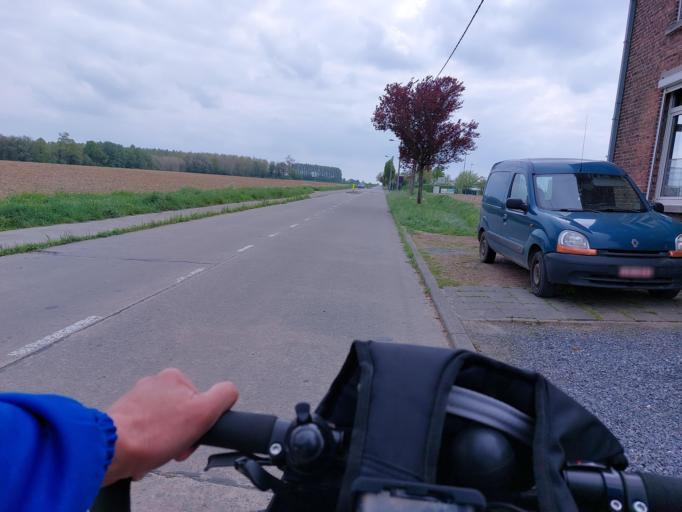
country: BE
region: Wallonia
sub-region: Province du Hainaut
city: Dour
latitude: 50.3609
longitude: 3.7352
